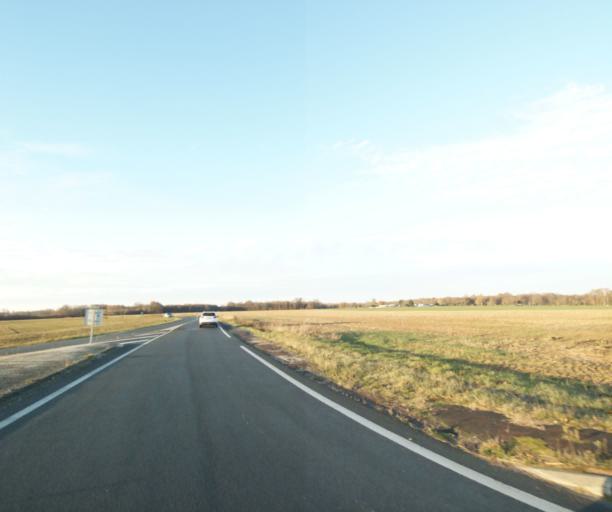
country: FR
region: Poitou-Charentes
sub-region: Departement de la Charente-Maritime
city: Nieul-les-Saintes
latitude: 45.8002
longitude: -0.7442
